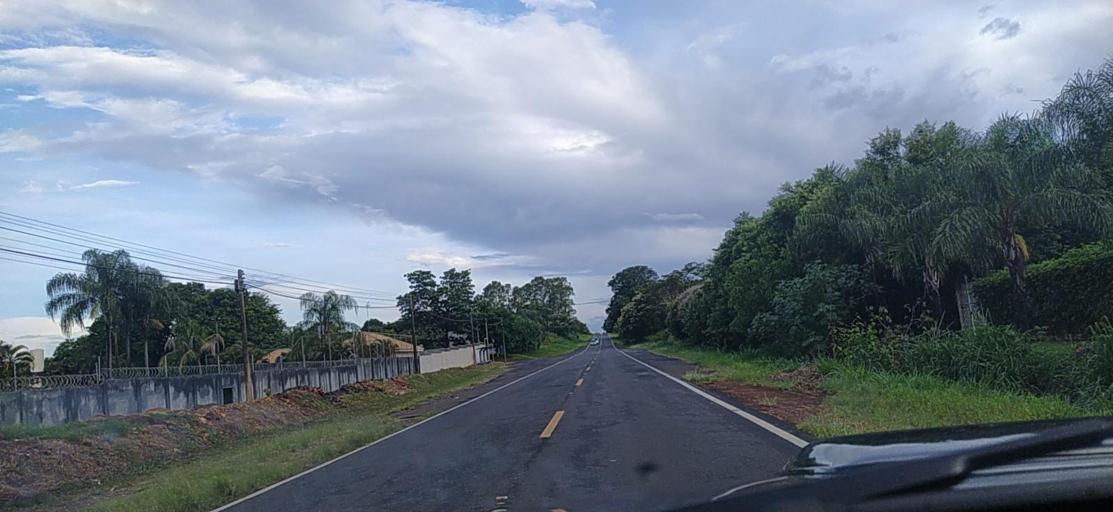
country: BR
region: Sao Paulo
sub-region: Pindorama
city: Pindorama
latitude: -21.1644
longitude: -48.9387
